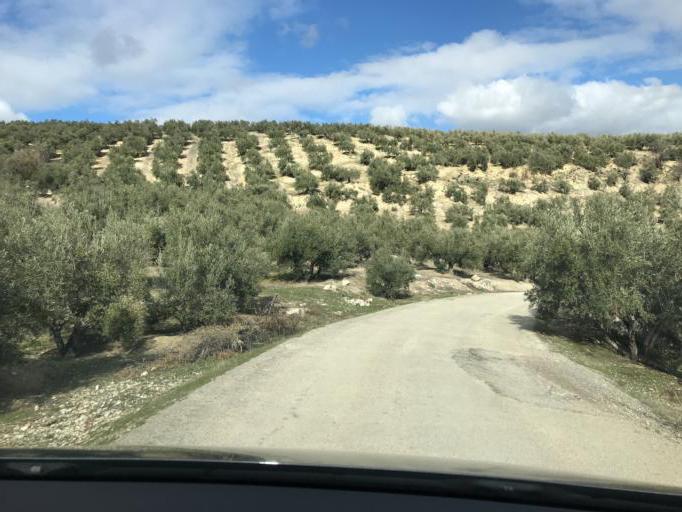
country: ES
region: Andalusia
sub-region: Provincia de Jaen
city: Jimena
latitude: 37.8117
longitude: -3.4497
